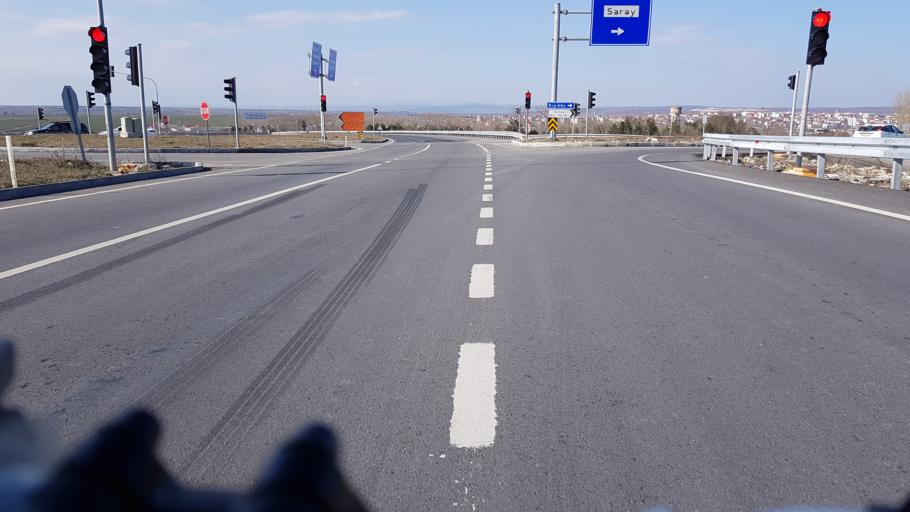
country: TR
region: Tekirdag
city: Saray
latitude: 41.4177
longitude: 27.9219
